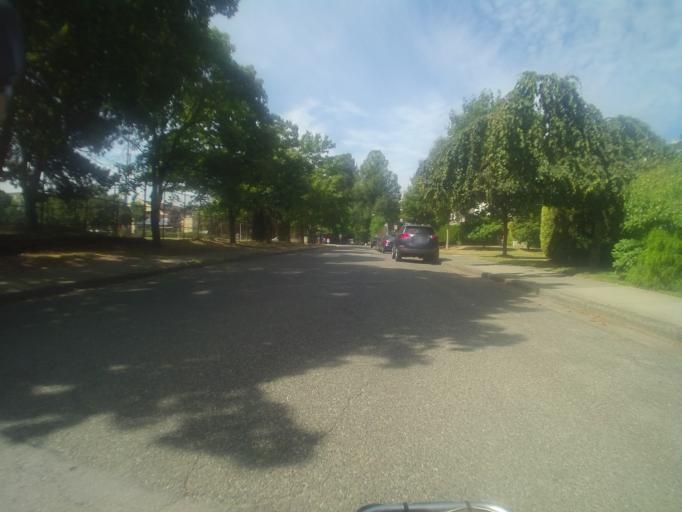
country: CA
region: British Columbia
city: West End
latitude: 49.2628
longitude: -123.1495
